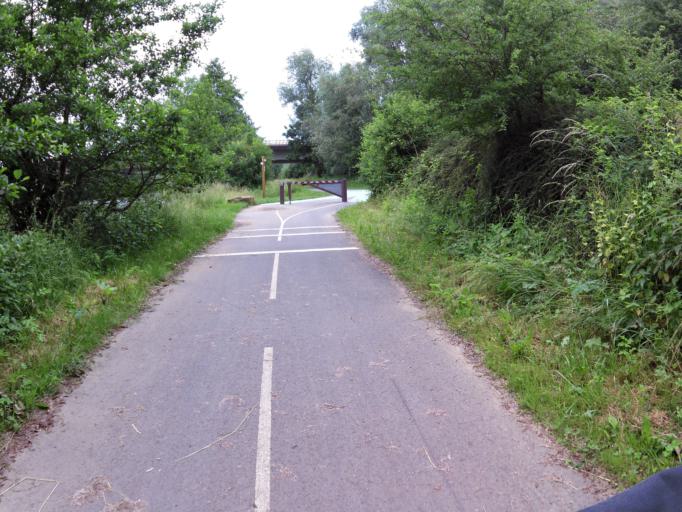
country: FR
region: Champagne-Ardenne
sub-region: Departement des Ardennes
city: Lumes
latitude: 49.7377
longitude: 4.7755
